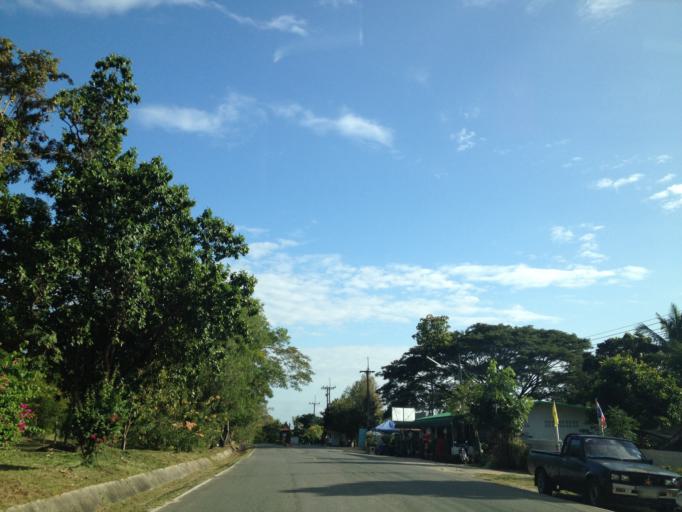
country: TH
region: Chiang Mai
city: Chiang Mai
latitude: 18.8648
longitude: 98.9462
